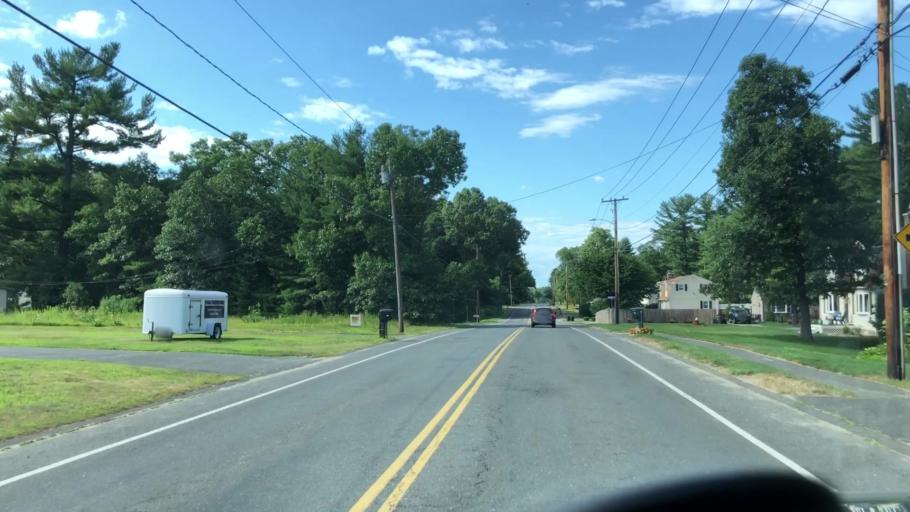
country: US
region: Massachusetts
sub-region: Hampshire County
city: Southampton
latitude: 42.2027
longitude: -72.6887
